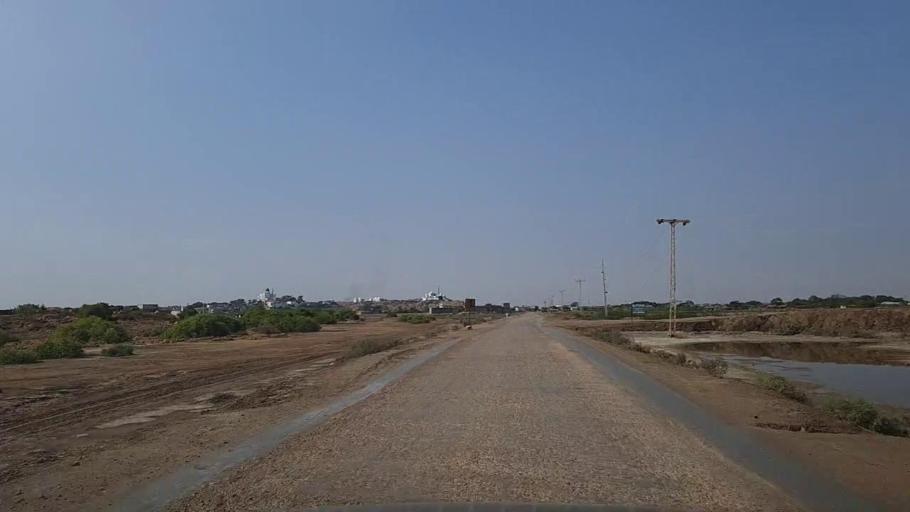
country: PK
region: Sindh
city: Thatta
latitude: 24.5554
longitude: 67.8882
